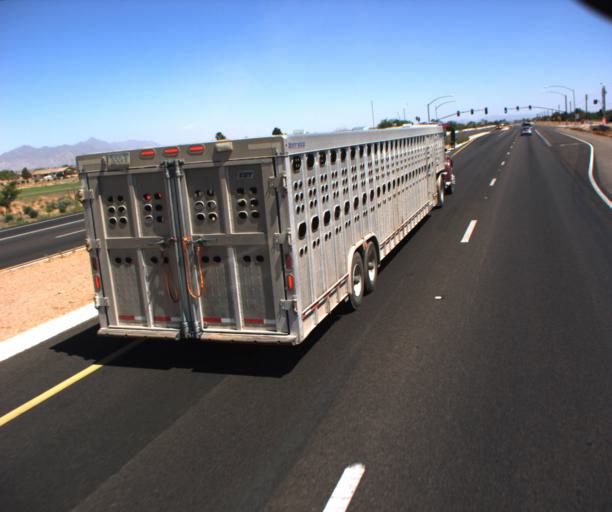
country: US
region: Arizona
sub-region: Pinal County
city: Maricopa
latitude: 33.0274
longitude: -112.0477
